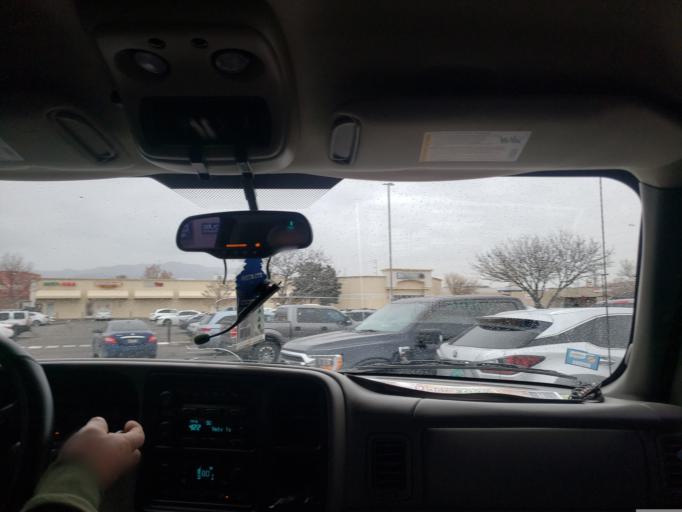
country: US
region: New Mexico
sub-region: Bernalillo County
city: North Valley
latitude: 35.1321
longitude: -106.5882
